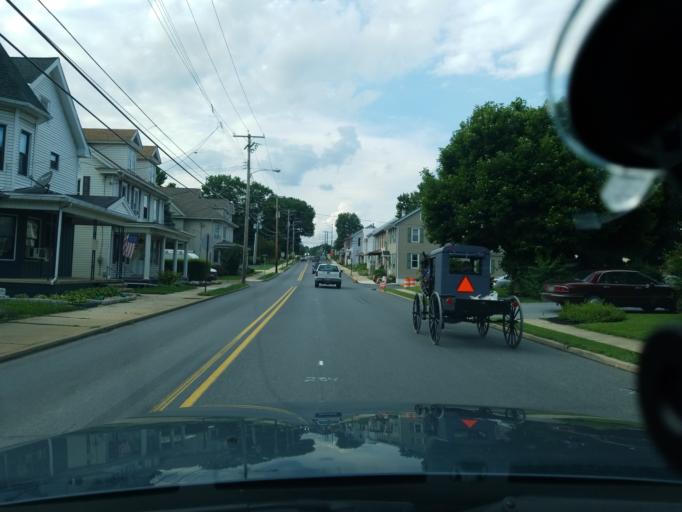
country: US
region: Pennsylvania
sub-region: Lebanon County
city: Myerstown
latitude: 40.3706
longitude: -76.3054
